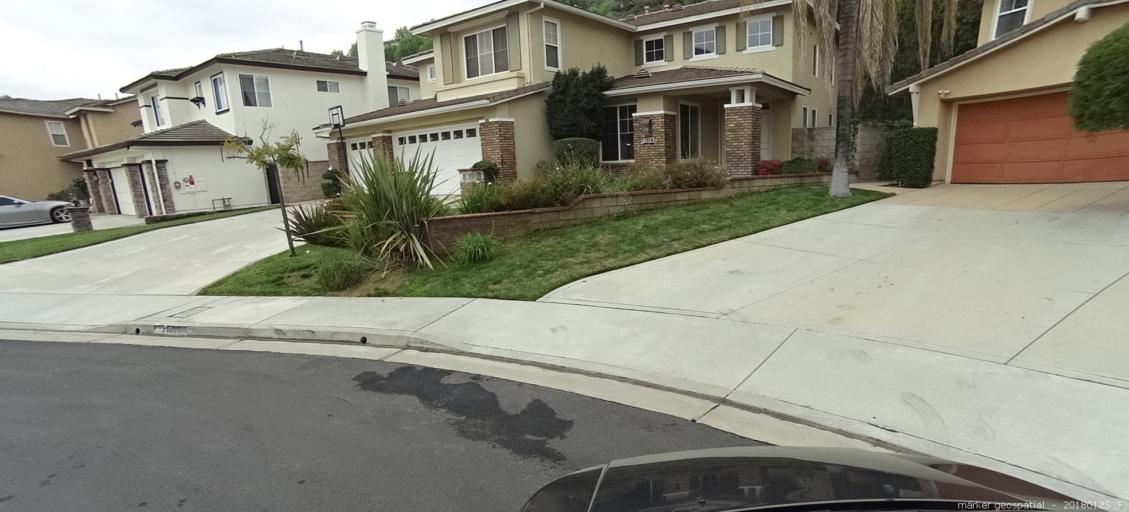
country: US
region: California
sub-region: Los Angeles County
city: Walnut
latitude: 33.9713
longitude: -117.8525
